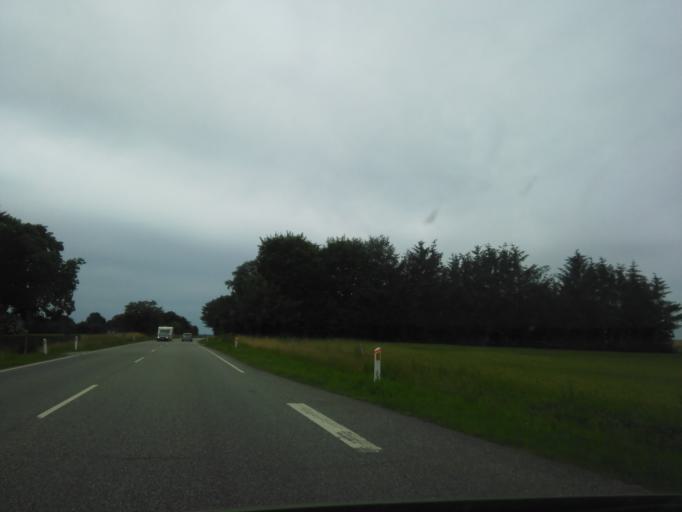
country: DK
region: Central Jutland
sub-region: Horsens Kommune
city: Horsens
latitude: 55.8920
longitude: 9.8675
